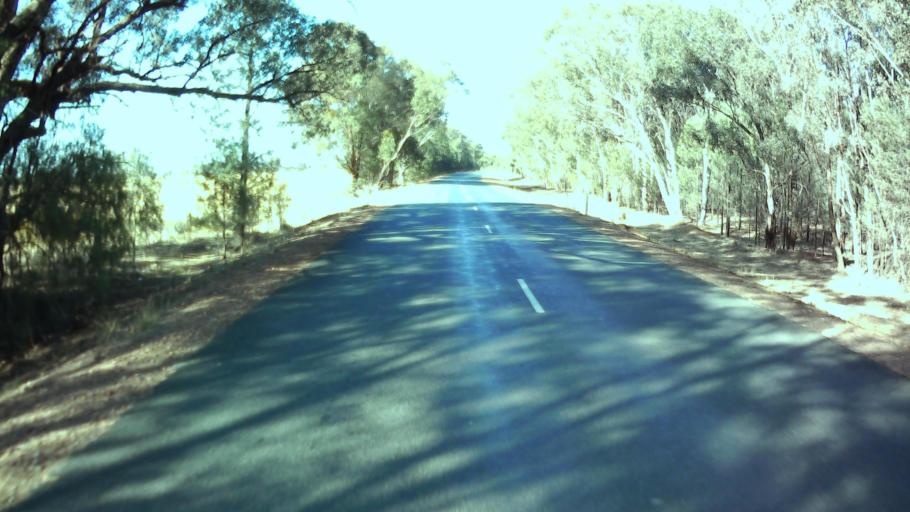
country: AU
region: New South Wales
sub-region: Weddin
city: Grenfell
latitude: -34.0116
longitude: 148.1169
